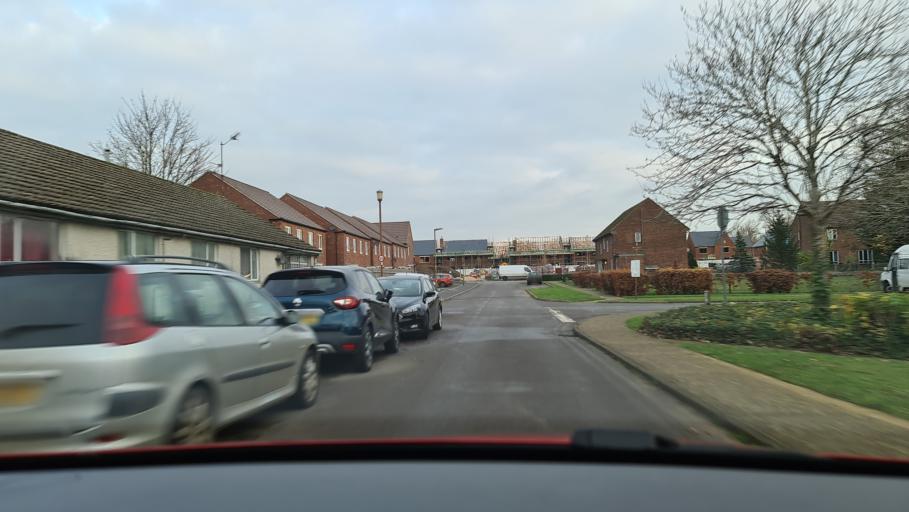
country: GB
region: England
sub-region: Oxfordshire
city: Somerton
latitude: 51.9273
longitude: -1.2602
